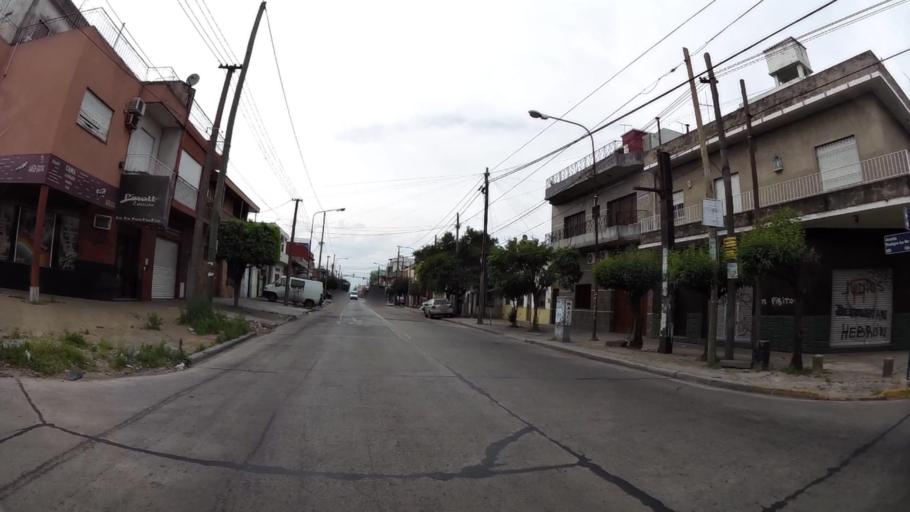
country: AR
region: Buenos Aires F.D.
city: Villa Lugano
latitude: -34.6909
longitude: -58.5169
